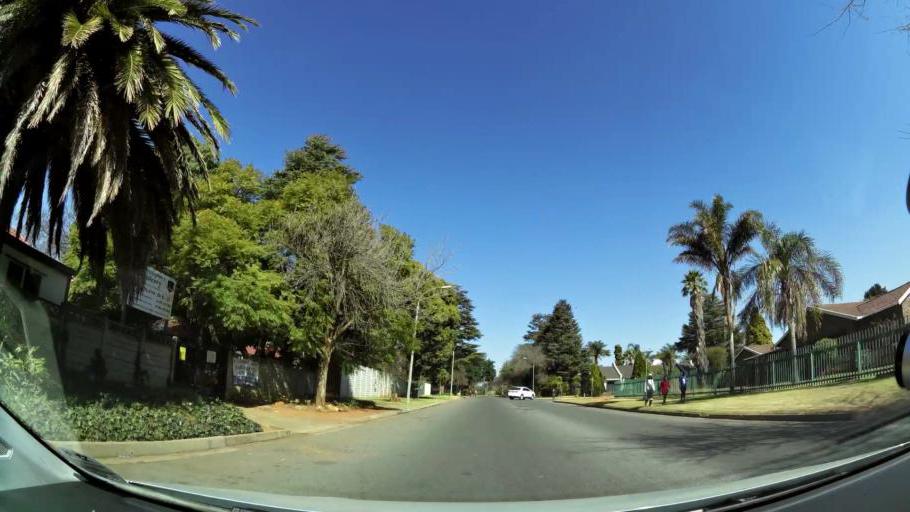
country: ZA
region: Gauteng
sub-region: City of Johannesburg Metropolitan Municipality
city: Modderfontein
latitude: -26.0620
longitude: 28.2120
